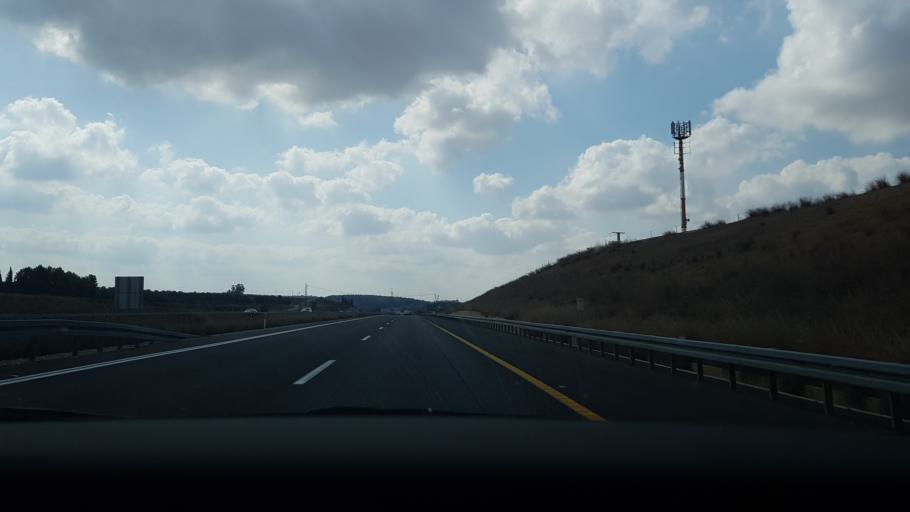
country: IL
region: Southern District
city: Qiryat Gat
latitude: 31.6151
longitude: 34.8140
